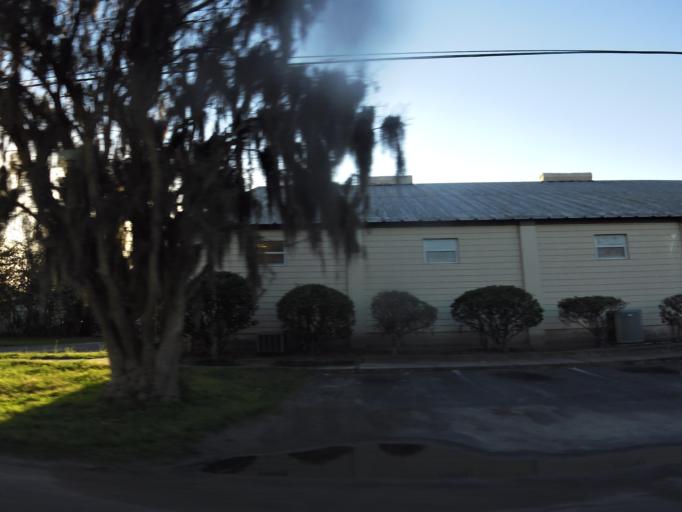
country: US
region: Florida
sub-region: Duval County
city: Jacksonville
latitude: 30.3380
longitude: -81.7099
